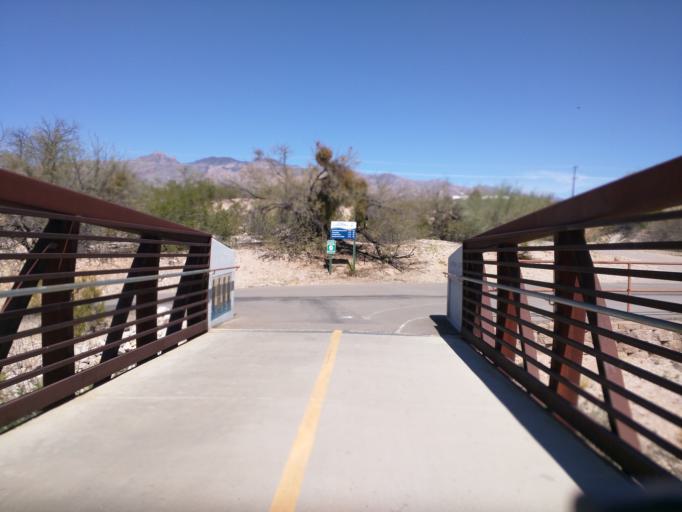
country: US
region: Arizona
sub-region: Pima County
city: Catalina Foothills
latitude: 32.2820
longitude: -110.9275
